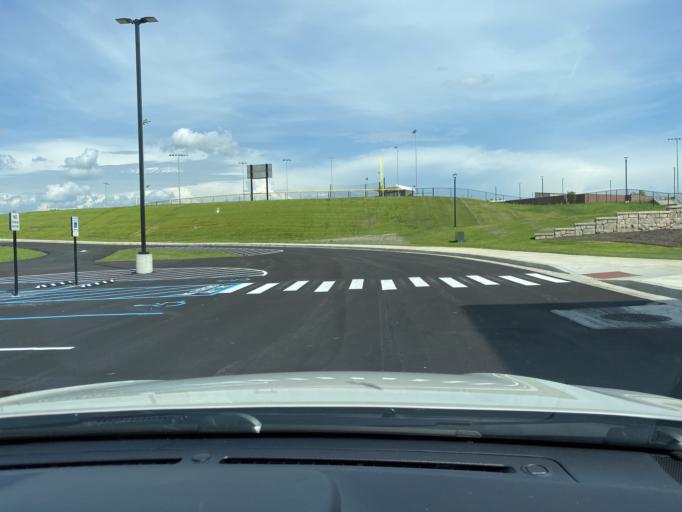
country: US
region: Kentucky
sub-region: Scott County
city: Georgetown
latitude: 38.2141
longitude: -84.6028
